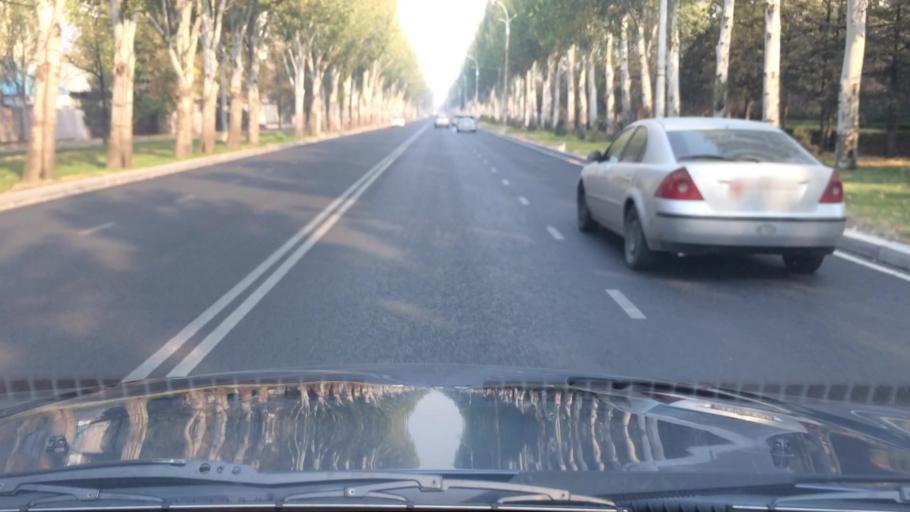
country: KG
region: Chuy
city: Bishkek
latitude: 42.8336
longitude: 74.5855
